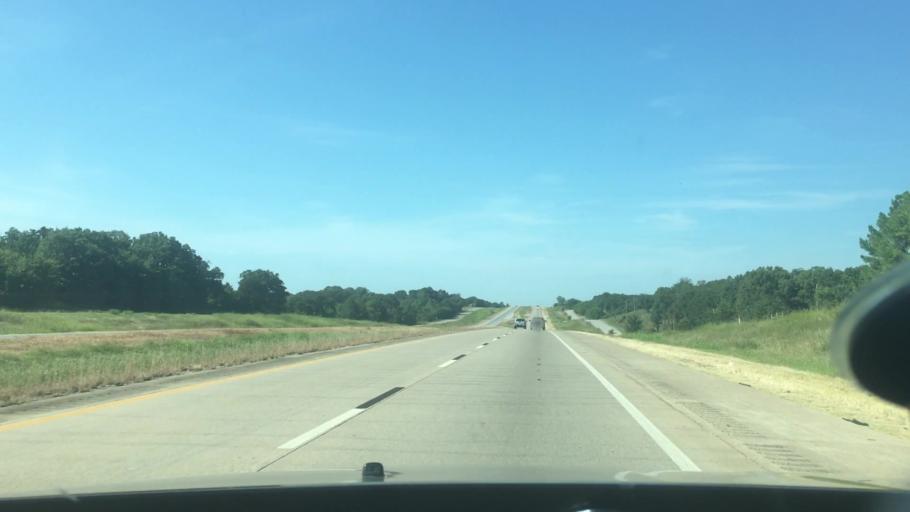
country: US
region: Oklahoma
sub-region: Atoka County
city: Atoka
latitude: 34.2944
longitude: -96.1925
